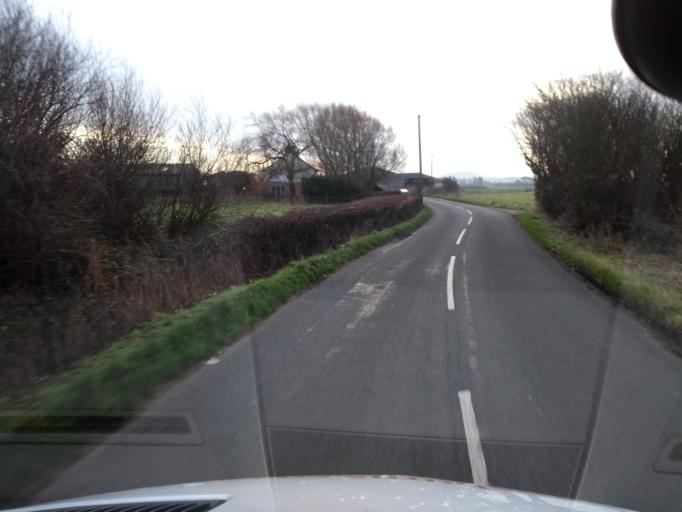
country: GB
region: England
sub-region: North Somerset
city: Bleadon
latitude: 51.2891
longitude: -2.9862
